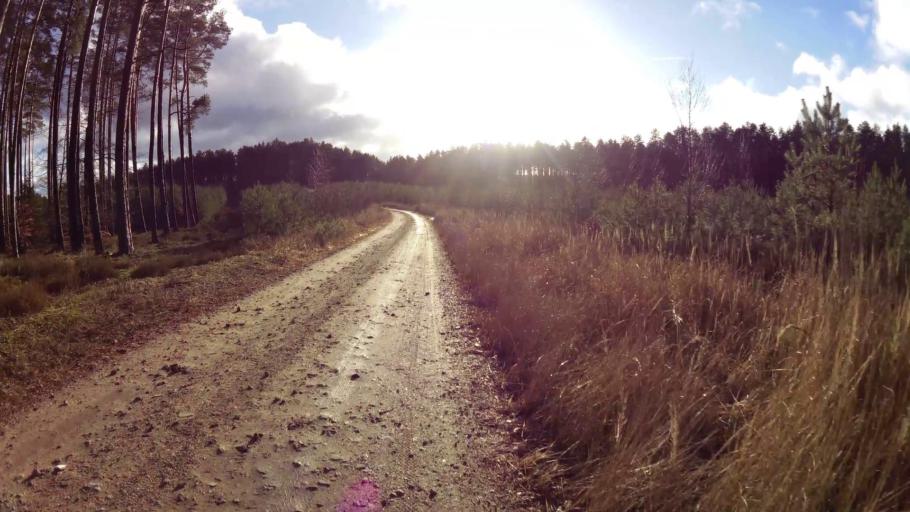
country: PL
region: West Pomeranian Voivodeship
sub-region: Powiat koszalinski
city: Sianow
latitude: 54.1080
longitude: 16.2973
